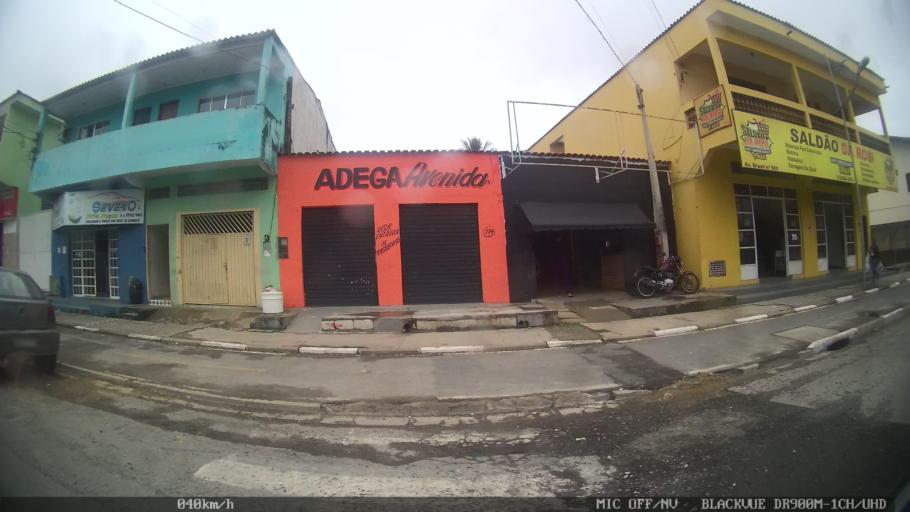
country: BR
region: Sao Paulo
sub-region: Juquia
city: Juquia
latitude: -24.3172
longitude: -47.6336
